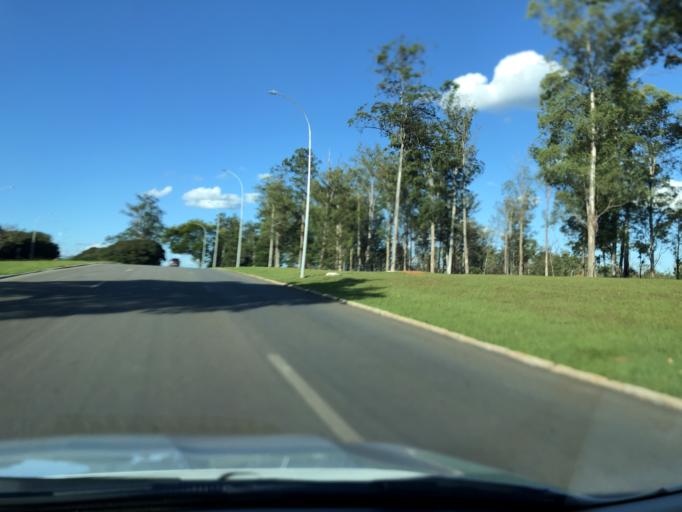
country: BR
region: Federal District
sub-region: Brasilia
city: Brasilia
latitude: -15.8472
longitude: -47.9306
